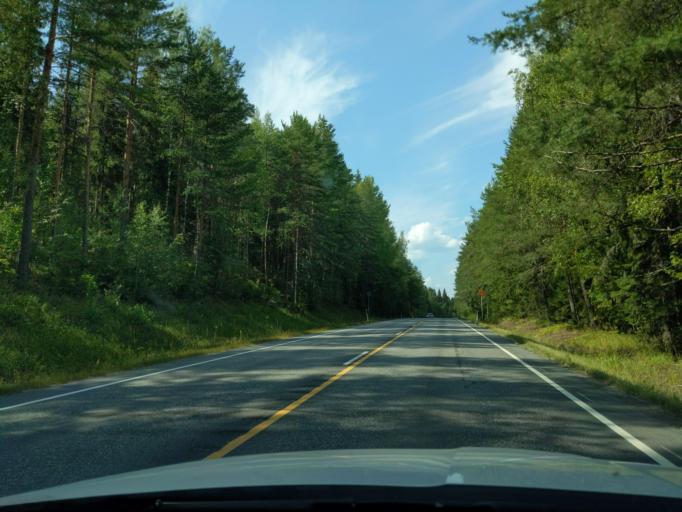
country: FI
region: Paijanne Tavastia
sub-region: Lahti
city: Padasjoki
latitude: 61.3768
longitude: 25.2022
